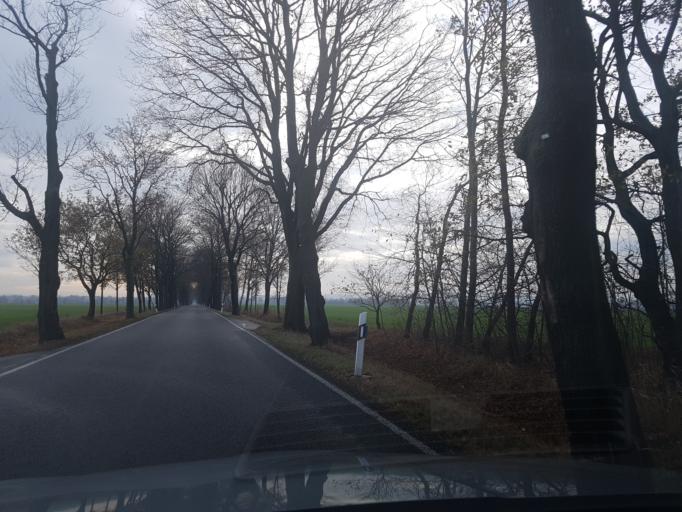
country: DE
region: Brandenburg
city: Plessa
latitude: 51.4281
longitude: 13.6239
